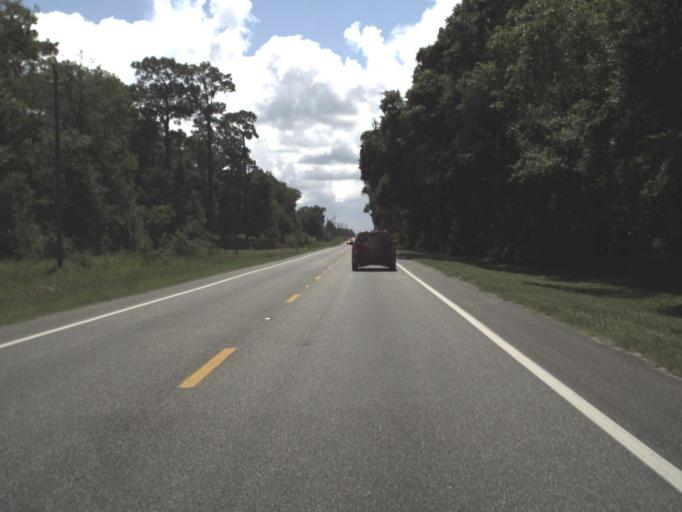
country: US
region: Florida
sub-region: Putnam County
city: Crescent City
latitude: 29.4871
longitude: -81.5719
